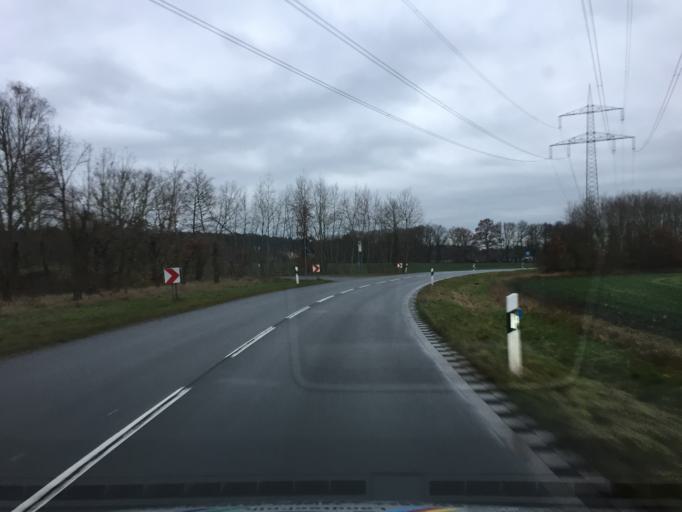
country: DE
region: Lower Saxony
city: Pennigsehl
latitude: 52.6218
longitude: 8.9969
